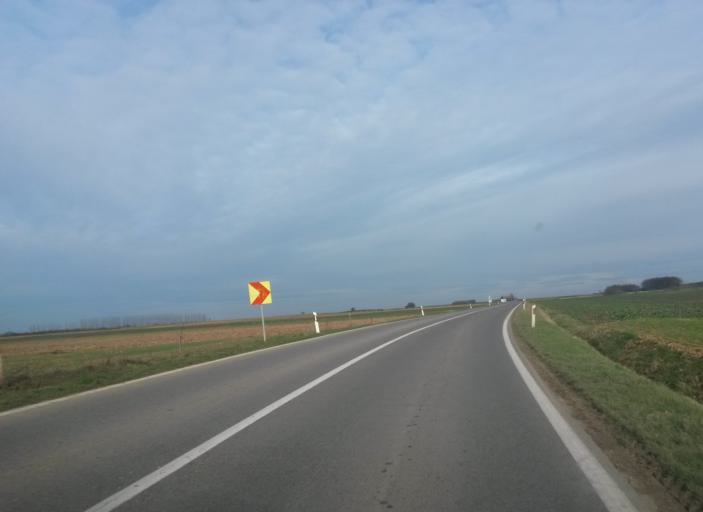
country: HR
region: Osjecko-Baranjska
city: Viskovci
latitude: 45.3610
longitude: 18.4265
